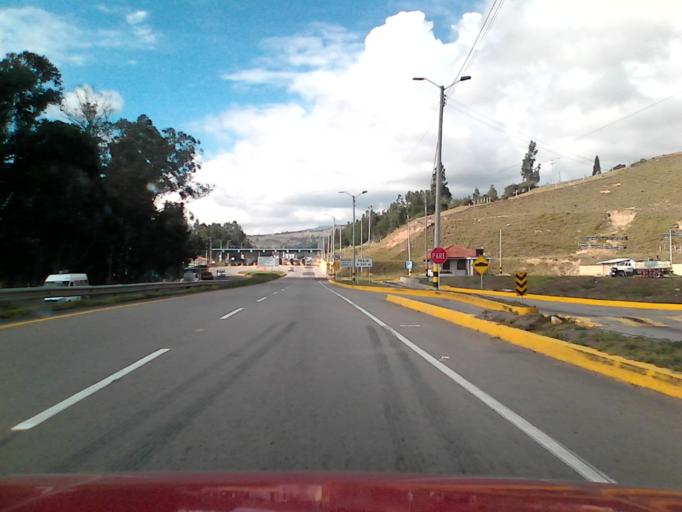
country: CO
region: Boyaca
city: Combita
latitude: 5.6593
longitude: -73.2762
